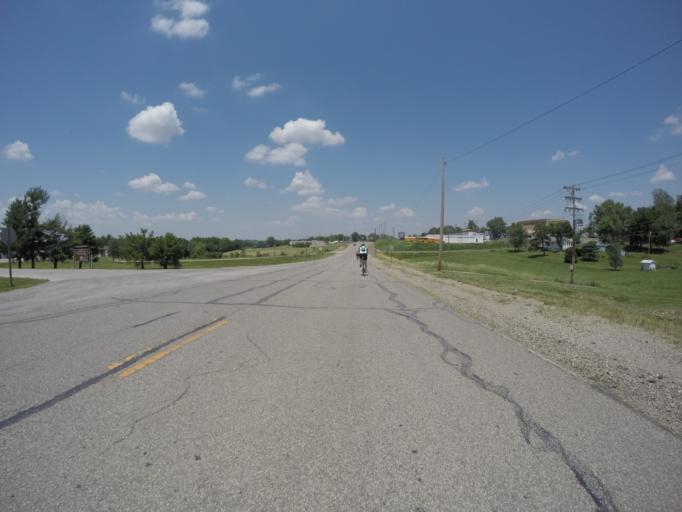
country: US
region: Kansas
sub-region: Doniphan County
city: Troy
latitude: 39.7823
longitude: -95.0971
